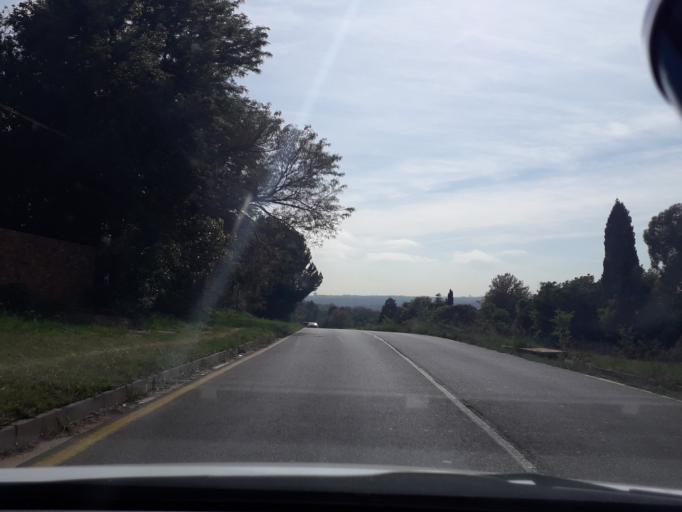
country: ZA
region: Gauteng
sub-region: City of Johannesburg Metropolitan Municipality
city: Roodepoort
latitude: -26.1180
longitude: 27.9384
